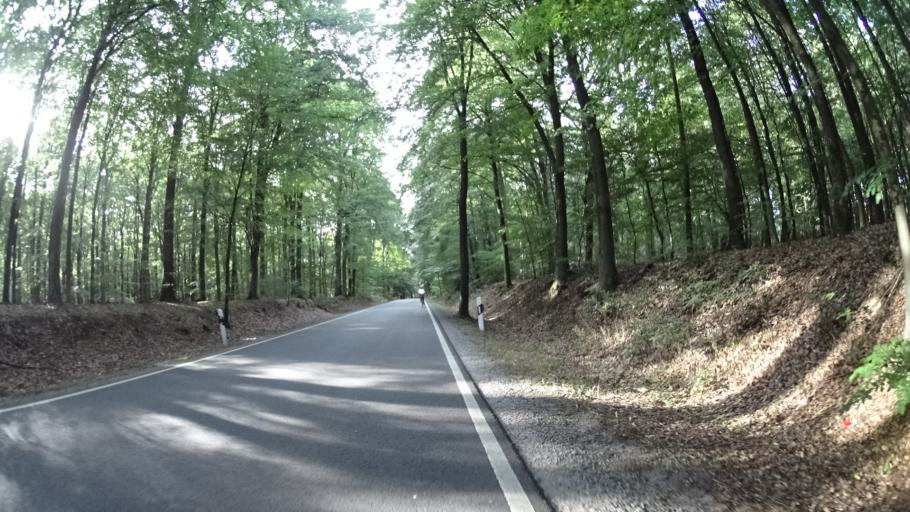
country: DE
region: Lower Saxony
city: Undeloh
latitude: 53.1575
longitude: 9.9044
